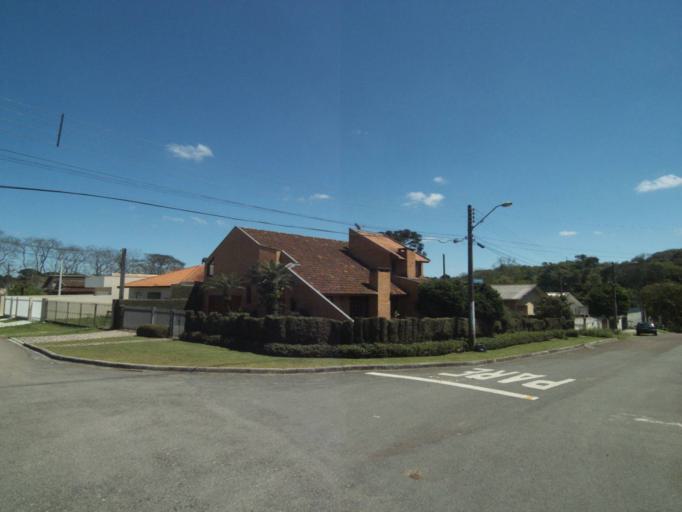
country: BR
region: Parana
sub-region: Curitiba
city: Curitiba
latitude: -25.3850
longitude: -49.2639
